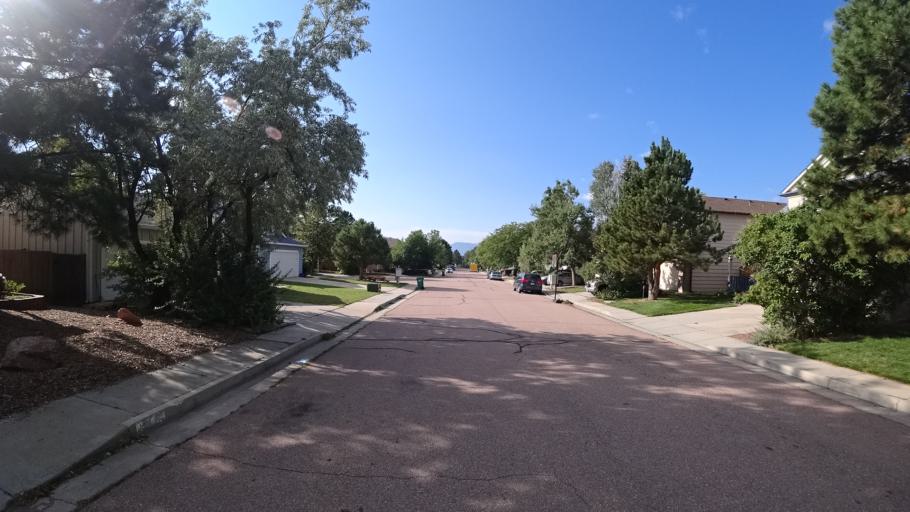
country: US
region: Colorado
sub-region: El Paso County
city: Air Force Academy
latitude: 38.9197
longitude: -104.8629
